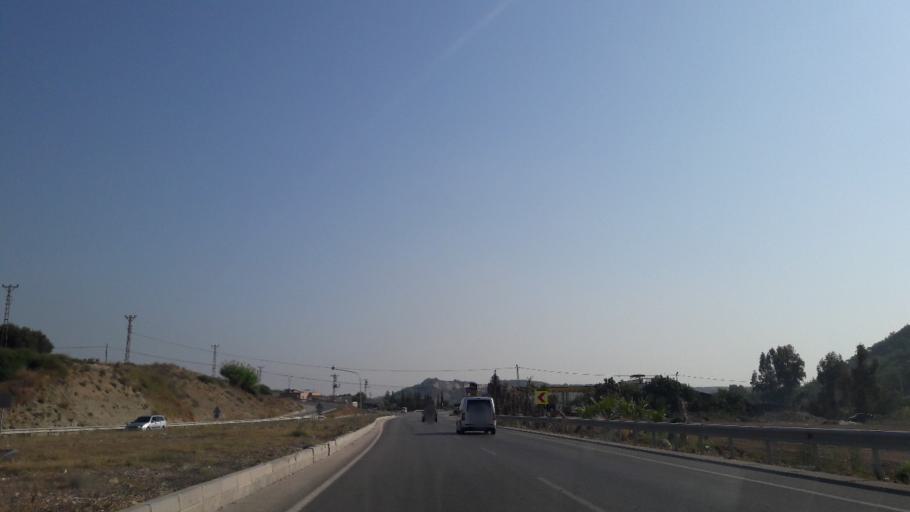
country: TR
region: Adana
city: Yuregir
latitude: 37.0704
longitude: 35.4570
